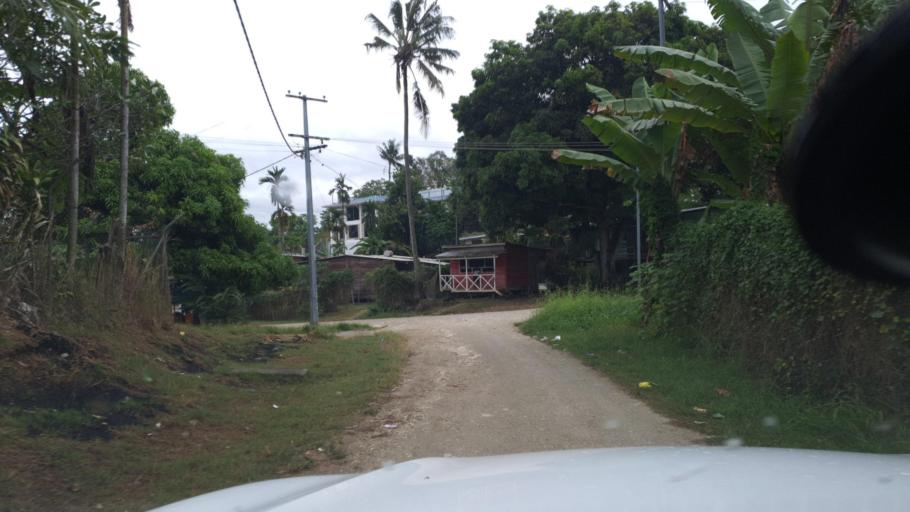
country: SB
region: Guadalcanal
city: Honiara
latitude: -9.4483
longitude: 159.9838
